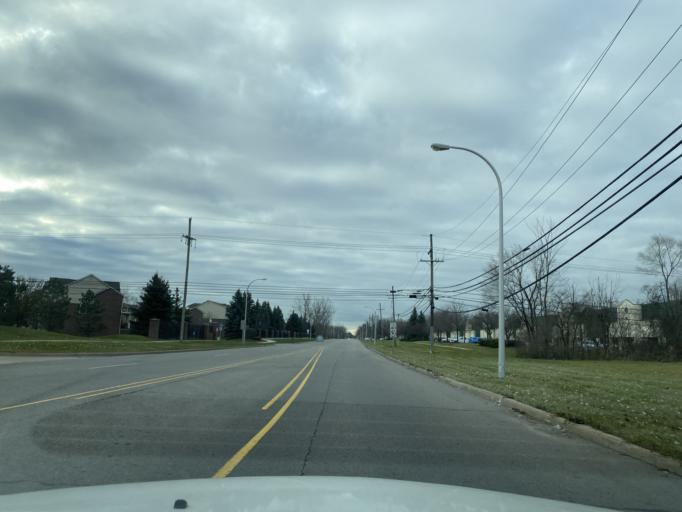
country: US
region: Michigan
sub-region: Wayne County
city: Taylor
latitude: 42.2101
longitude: -83.2877
